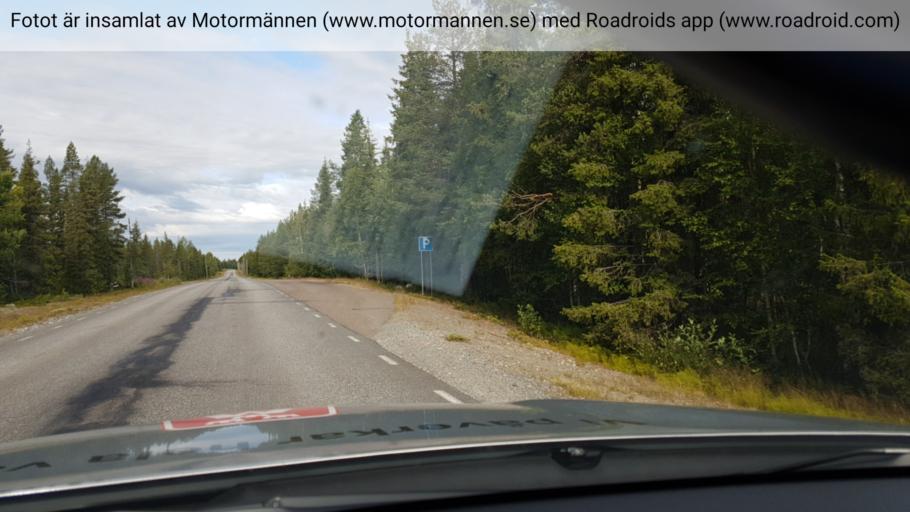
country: SE
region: Vaesterbotten
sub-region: Skelleftea Kommun
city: Storvik
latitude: 65.3579
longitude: 20.4566
